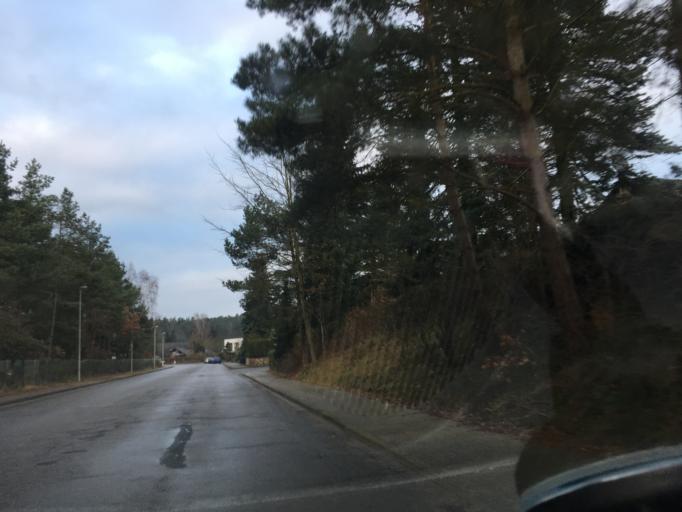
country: DE
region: Lower Saxony
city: Adendorf
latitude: 53.2799
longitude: 10.4247
